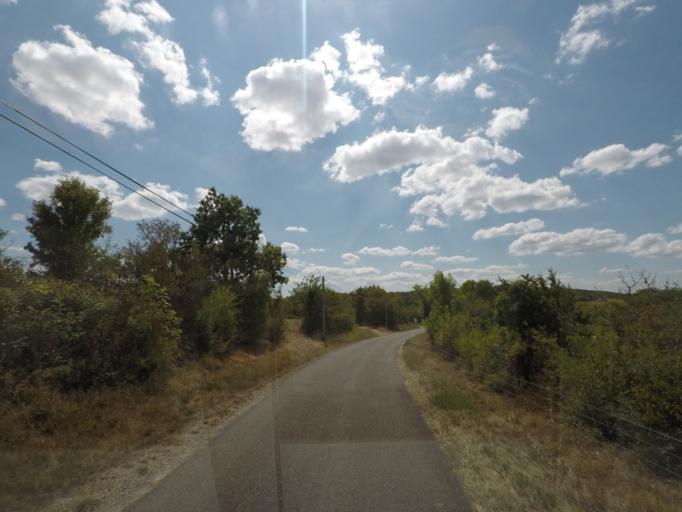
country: FR
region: Midi-Pyrenees
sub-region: Departement du Lot
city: Cajarc
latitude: 44.5407
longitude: 1.6707
